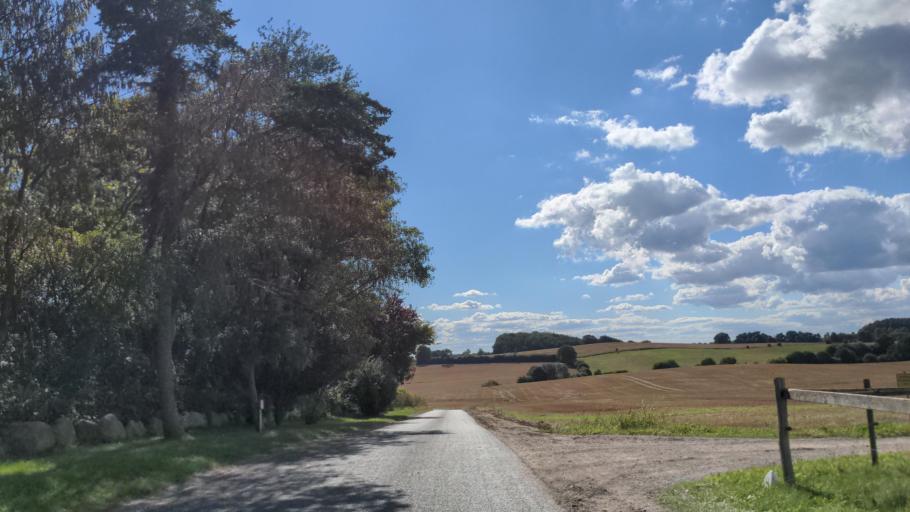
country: DE
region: Schleswig-Holstein
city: Kasseedorf
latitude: 54.1325
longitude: 10.7212
